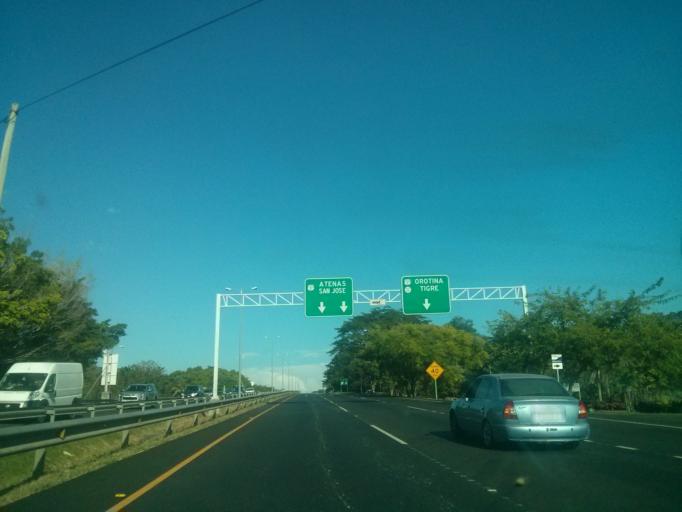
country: CR
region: Alajuela
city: Orotina
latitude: 9.9055
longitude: -84.5244
